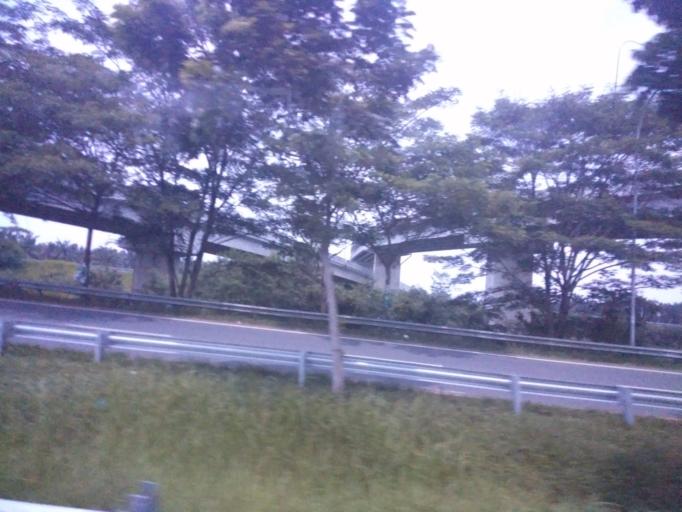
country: ID
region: North Sumatra
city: Percut
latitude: 3.5992
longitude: 98.8426
